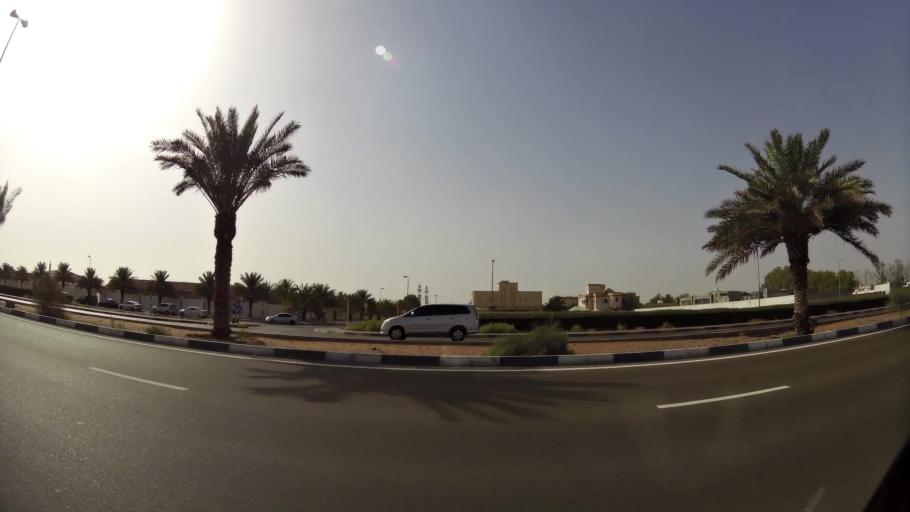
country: AE
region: Abu Dhabi
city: Al Ain
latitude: 24.2310
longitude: 55.6730
